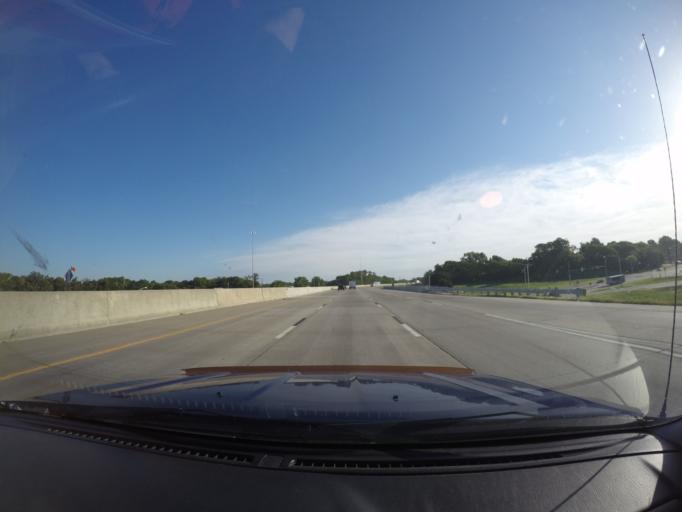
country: US
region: Kansas
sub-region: Wyandotte County
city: Kansas City
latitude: 39.1160
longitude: -94.6817
